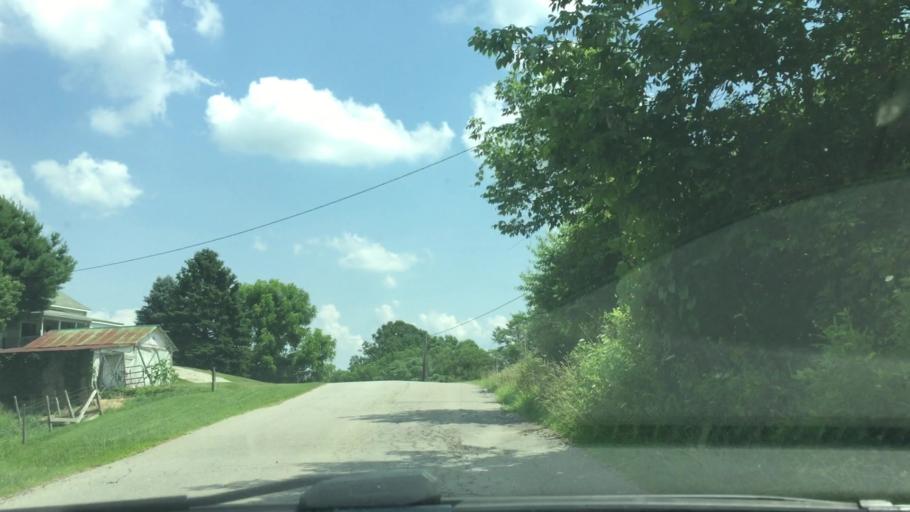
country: US
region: West Virginia
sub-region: Wetzel County
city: New Martinsville
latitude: 39.7247
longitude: -80.7549
